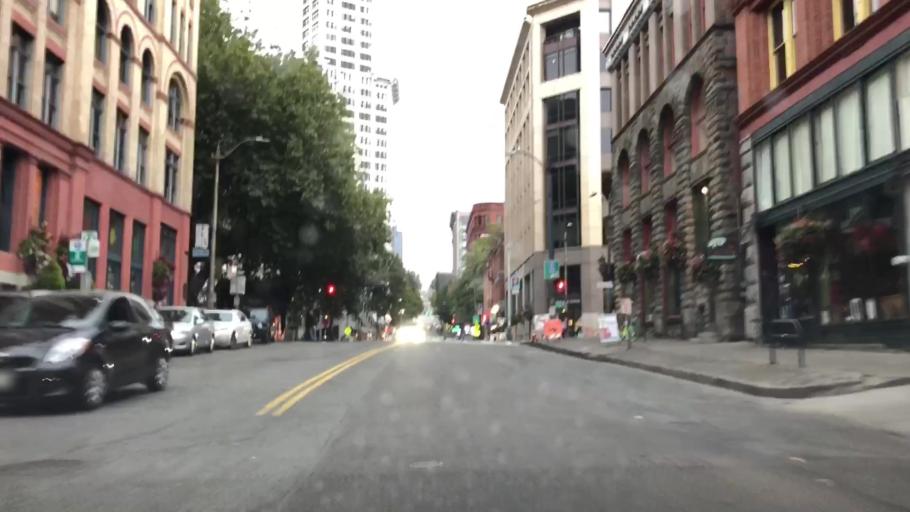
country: US
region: Washington
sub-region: Kitsap County
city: Manchester
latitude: 47.5699
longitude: -122.5108
